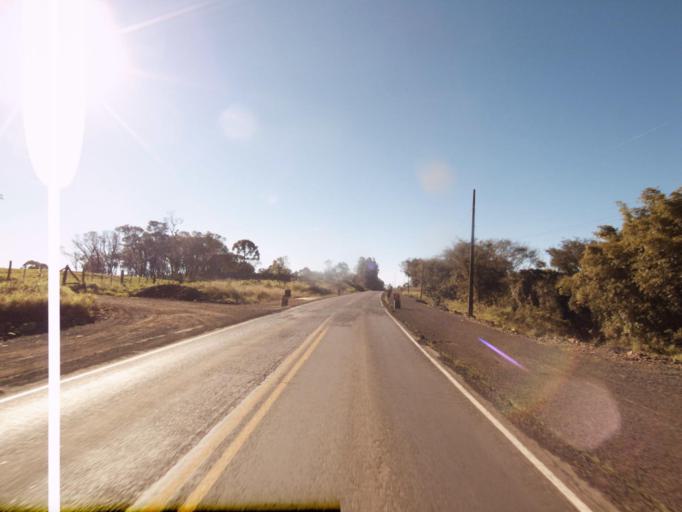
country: AR
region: Misiones
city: Bernardo de Irigoyen
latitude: -26.6697
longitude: -53.5197
